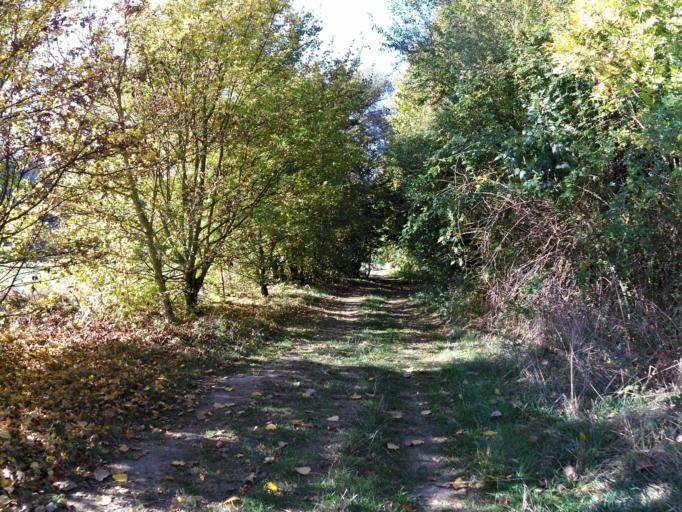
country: DE
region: Bavaria
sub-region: Regierungsbezirk Unterfranken
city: Eibelstadt
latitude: 49.7223
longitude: 9.9934
